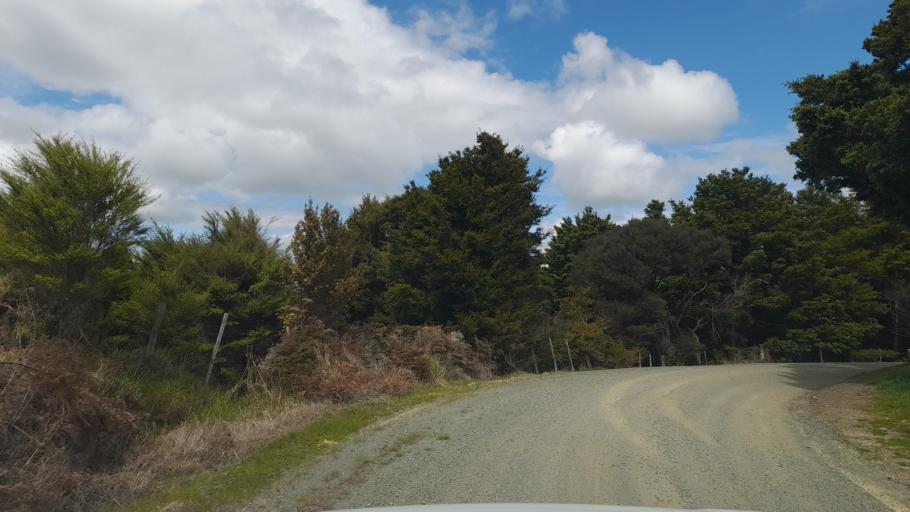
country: NZ
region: Auckland
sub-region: Auckland
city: Wellsford
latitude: -36.2093
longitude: 174.3340
